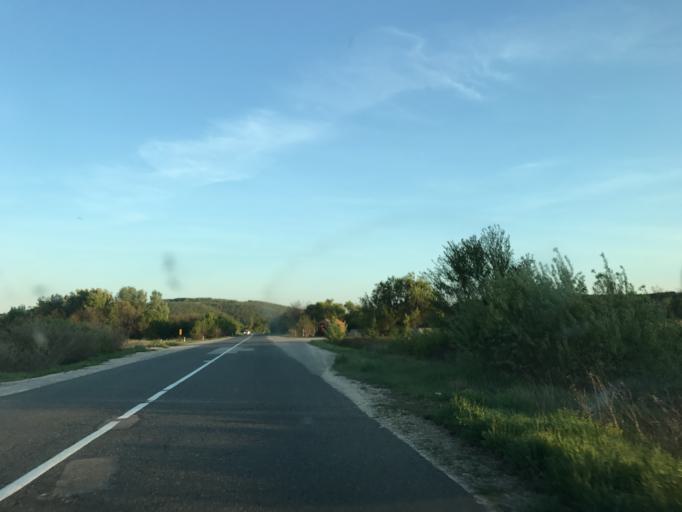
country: RO
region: Mehedinti
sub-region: Comuna Gogosu
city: Ostrovu Mare
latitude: 44.4391
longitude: 22.4577
